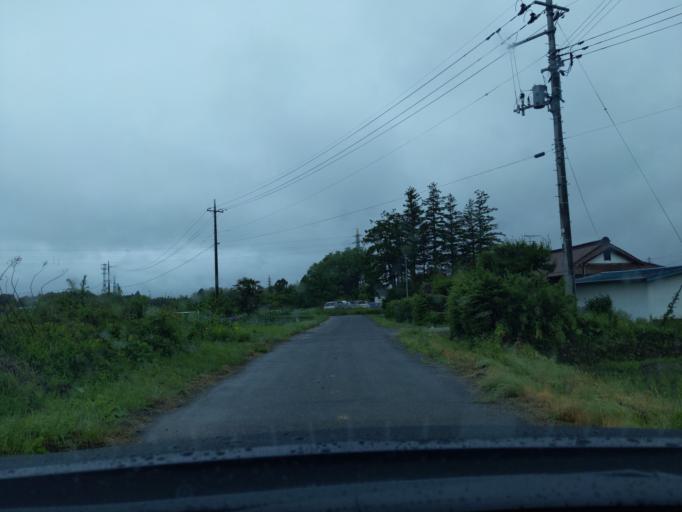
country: JP
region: Fukushima
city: Koriyama
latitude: 37.4485
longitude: 140.3295
